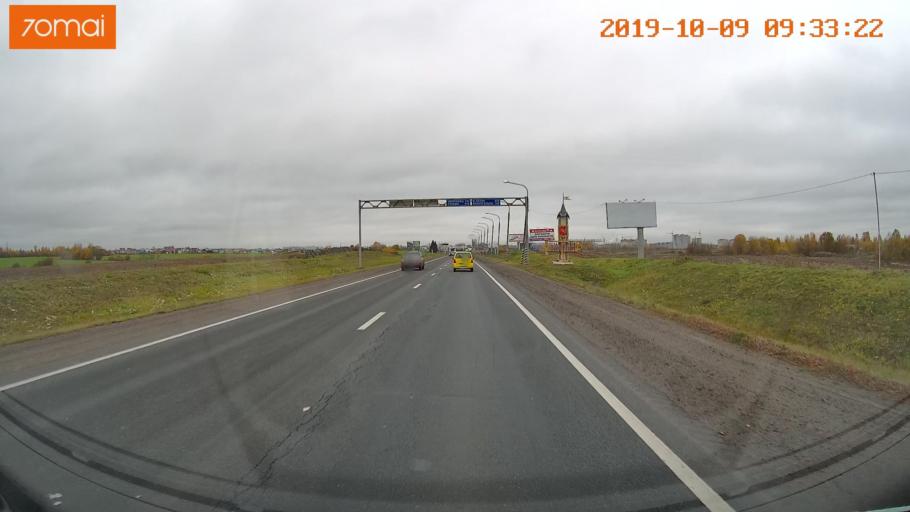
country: RU
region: Vologda
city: Vologda
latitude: 59.1674
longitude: 39.9153
